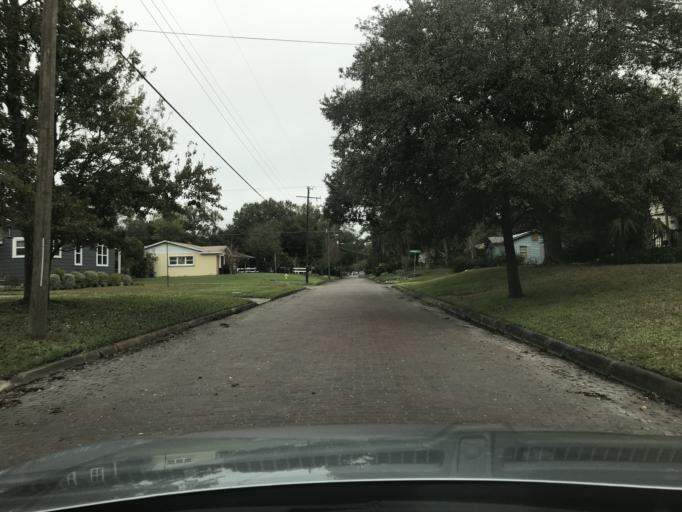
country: US
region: Florida
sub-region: Hillsborough County
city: Tampa
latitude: 27.9780
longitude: -82.4743
